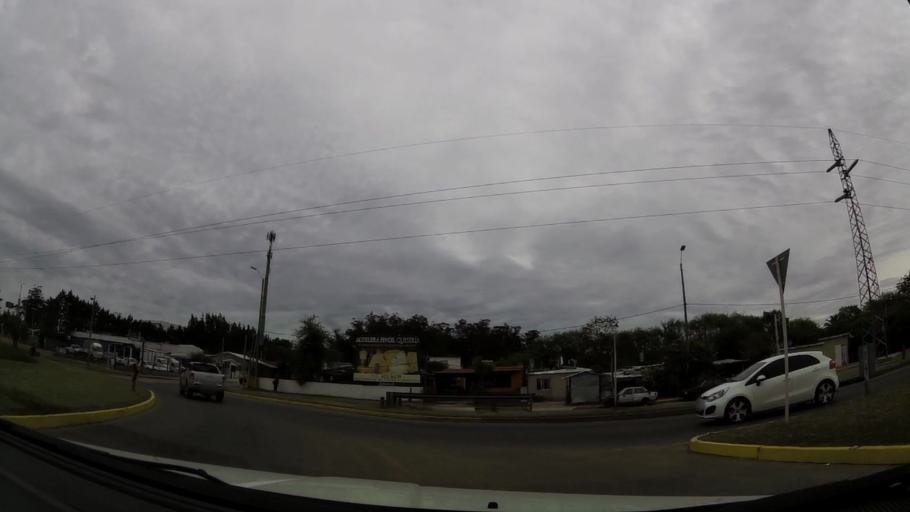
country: UY
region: Maldonado
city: Maldonado
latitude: -34.9146
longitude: -54.9449
